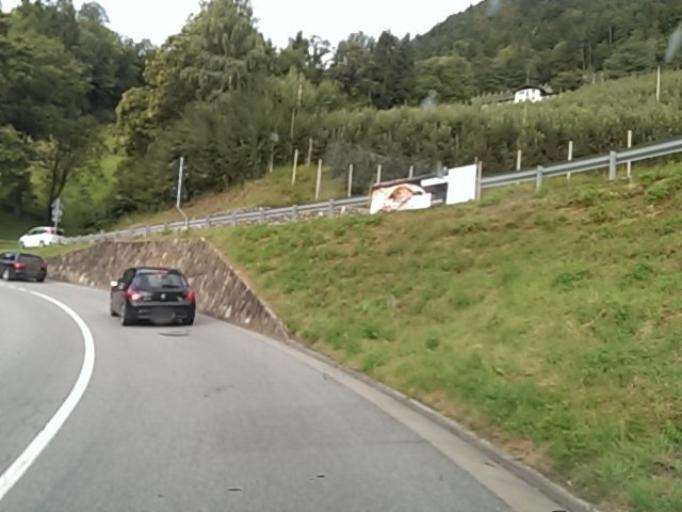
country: IT
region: Trentino-Alto Adige
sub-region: Bolzano
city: San Pancrazio
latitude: 46.6076
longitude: 11.1108
